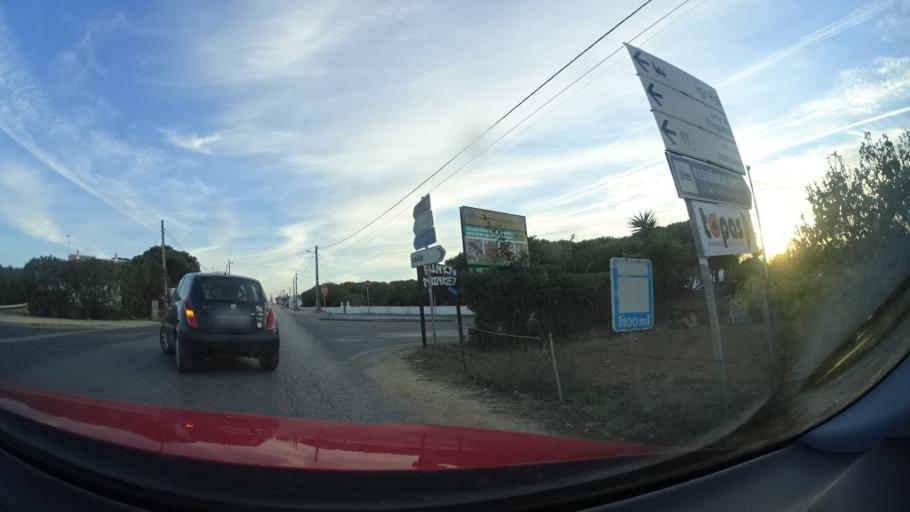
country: PT
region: Faro
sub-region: Vila do Bispo
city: Sagres
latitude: 37.0118
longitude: -8.9437
